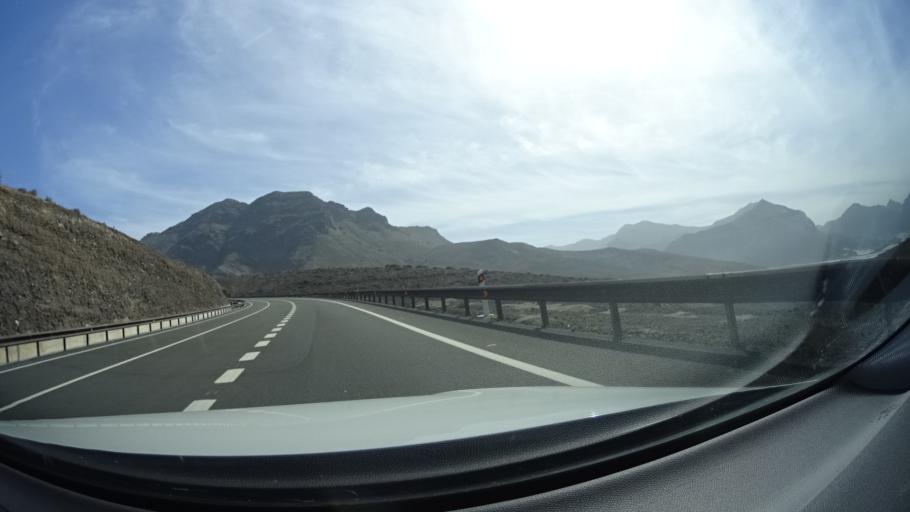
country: ES
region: Canary Islands
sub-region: Provincia de Las Palmas
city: San Nicolas
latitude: 28.0124
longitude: -15.7775
